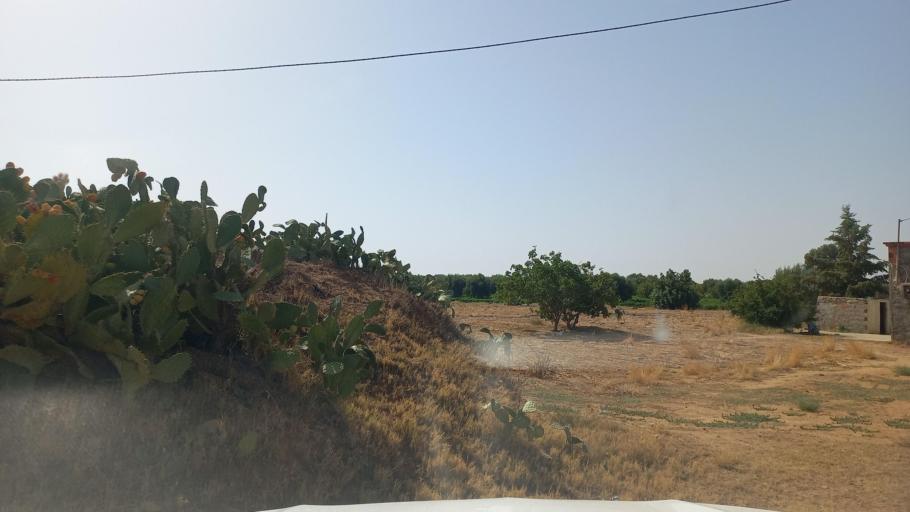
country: TN
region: Al Qasrayn
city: Kasserine
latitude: 35.2352
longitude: 9.0500
